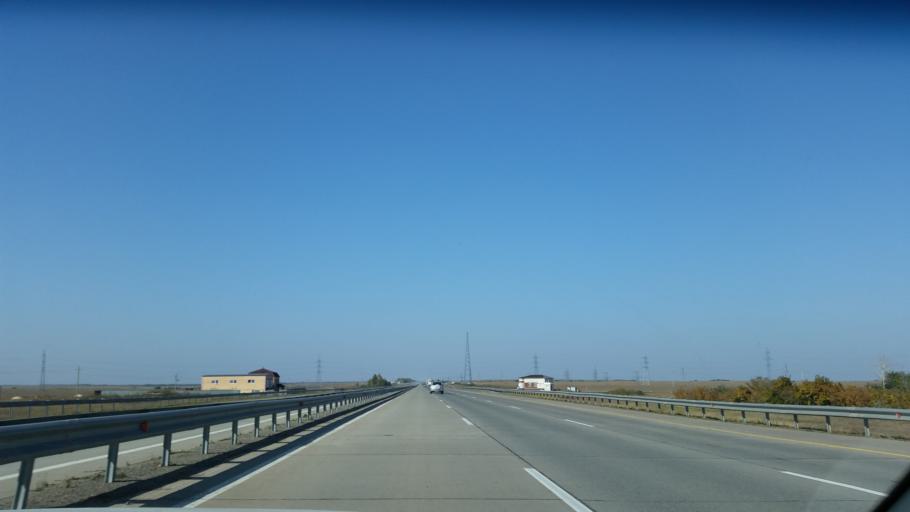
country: KZ
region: Astana Qalasy
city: Astana
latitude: 51.2868
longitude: 71.3610
